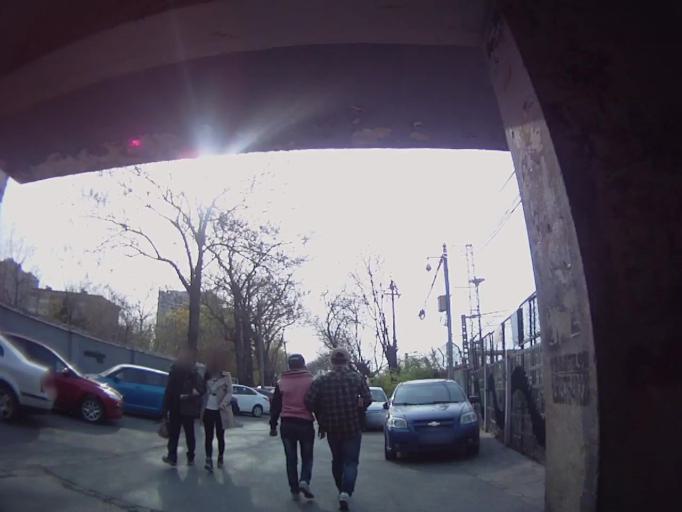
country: CN
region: Beijing
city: Chaowai
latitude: 39.8998
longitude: 116.4425
